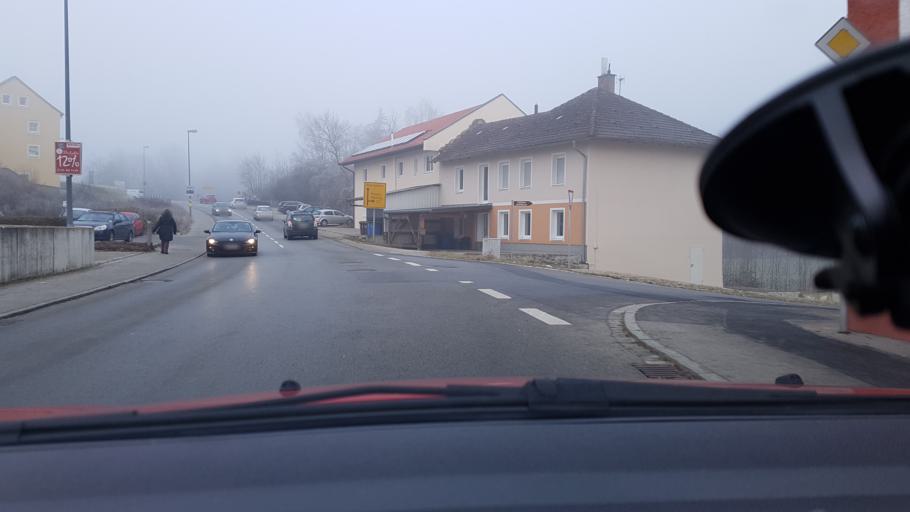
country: DE
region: Bavaria
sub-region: Lower Bavaria
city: Simbach am Inn
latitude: 48.2695
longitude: 13.0231
